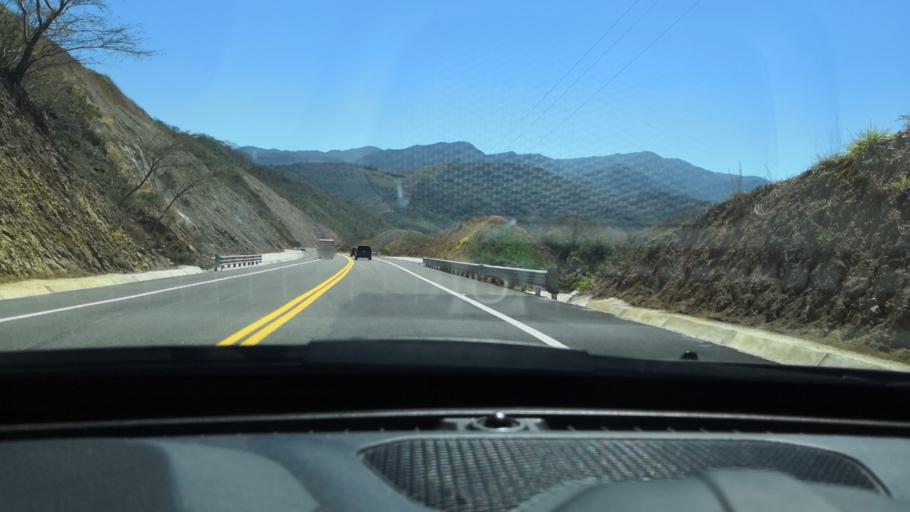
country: MX
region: Nayarit
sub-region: Compostela
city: Juan Escutia (Borbollon)
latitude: 21.1457
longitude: -104.9097
